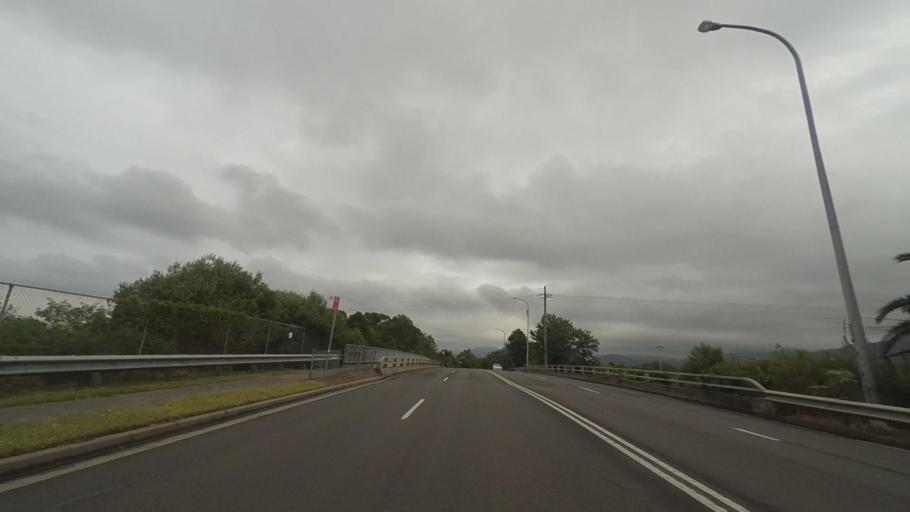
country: AU
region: New South Wales
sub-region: Wollongong
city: Gwynneville
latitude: -34.4194
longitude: 150.8904
